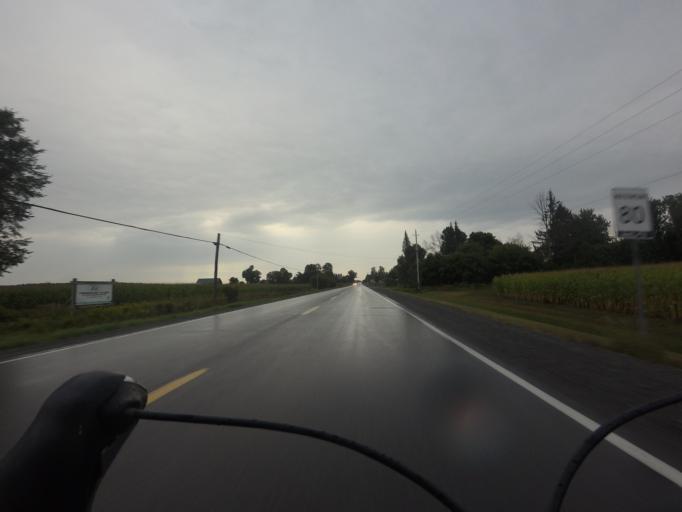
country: CA
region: Ontario
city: Bells Corners
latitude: 45.1986
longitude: -75.6914
